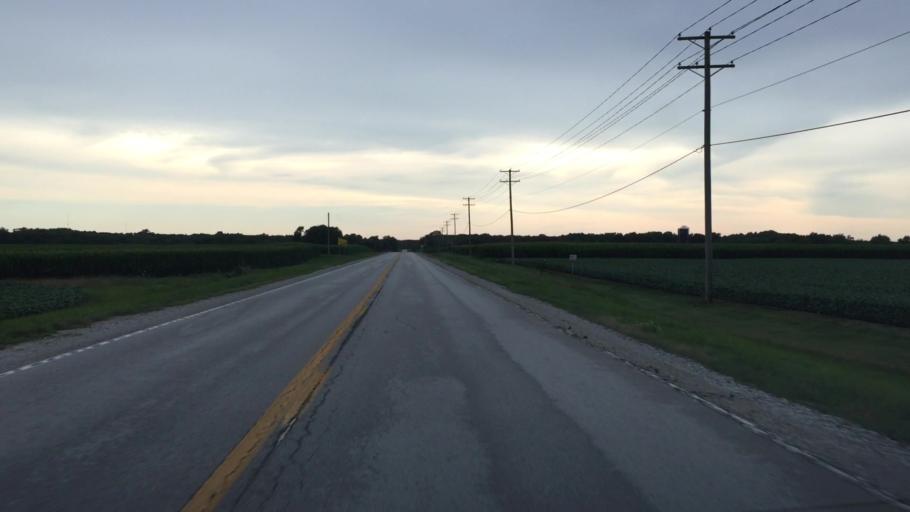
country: US
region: Iowa
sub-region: Lee County
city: Keokuk
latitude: 40.3607
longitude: -91.3658
